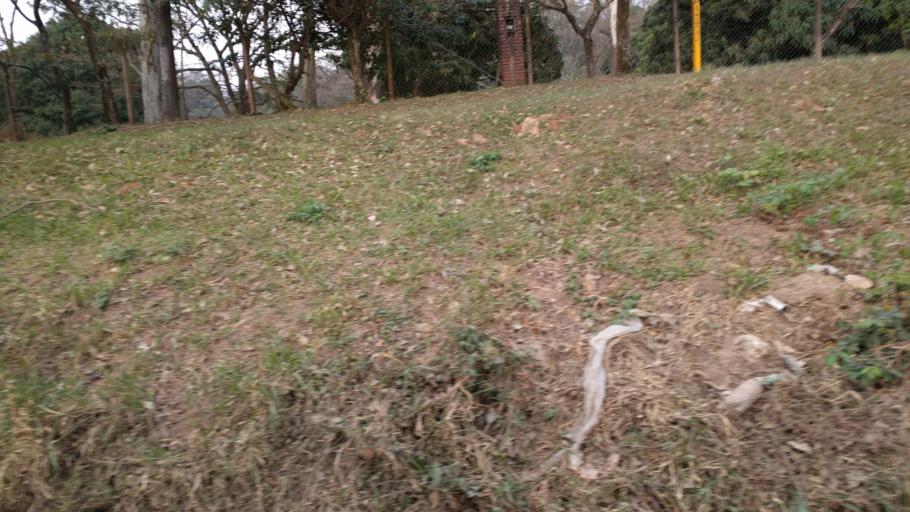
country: BO
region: Santa Cruz
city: Santa Rita
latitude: -17.9168
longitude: -63.3468
